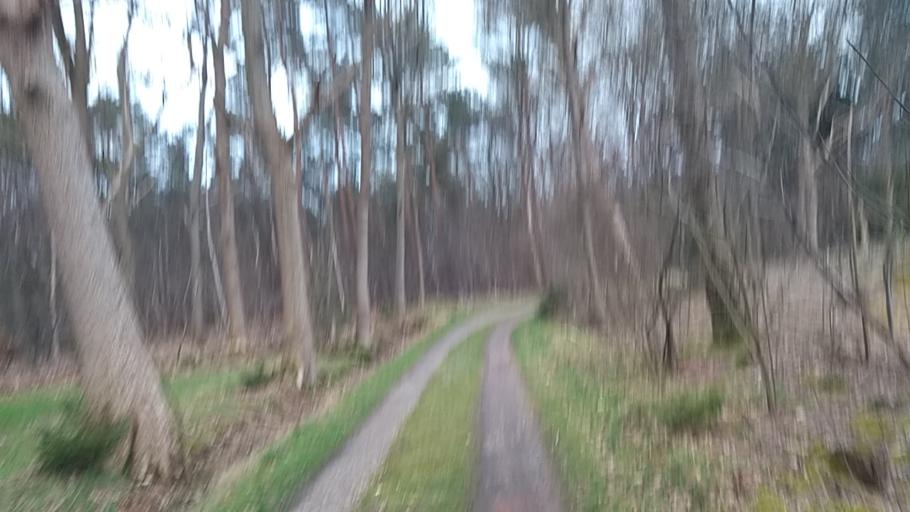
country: NL
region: Overijssel
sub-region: Gemeente Almelo
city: Almelo
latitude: 52.3550
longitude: 6.7196
